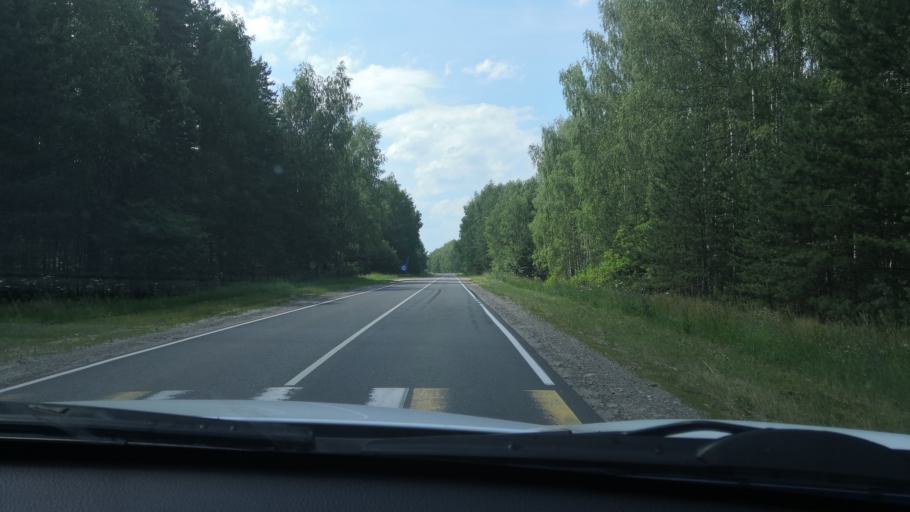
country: RU
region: Rjazan
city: Murmino
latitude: 54.5406
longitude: 40.1720
